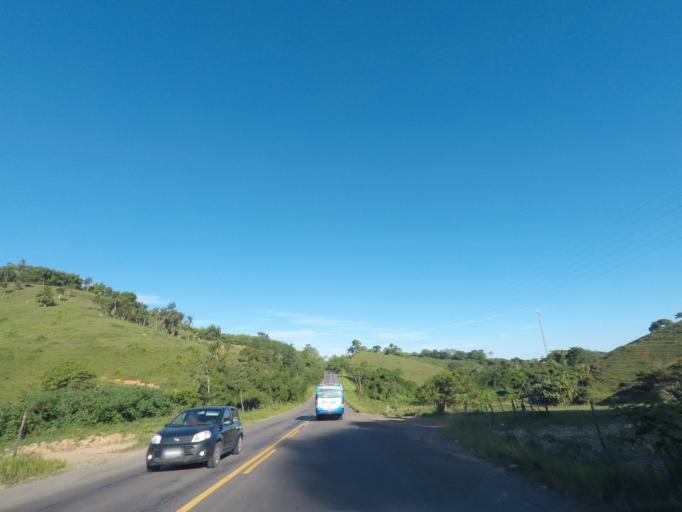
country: BR
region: Bahia
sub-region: Nazare
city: Nazare
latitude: -13.0288
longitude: -39.0088
